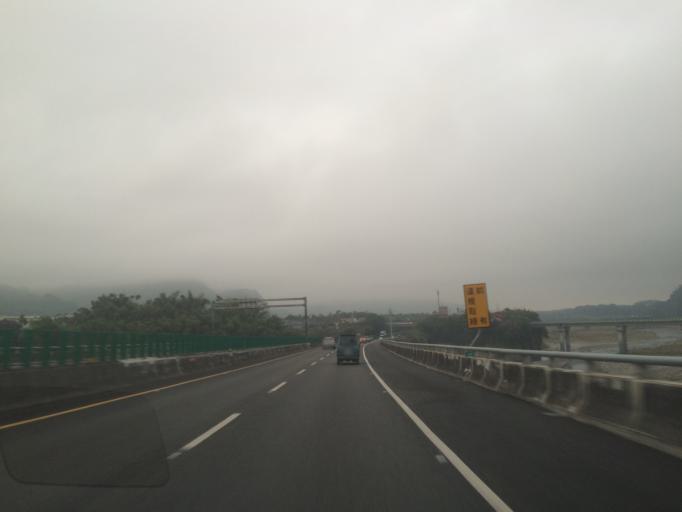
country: TW
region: Taiwan
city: Zhongxing New Village
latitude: 23.9887
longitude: 120.7977
